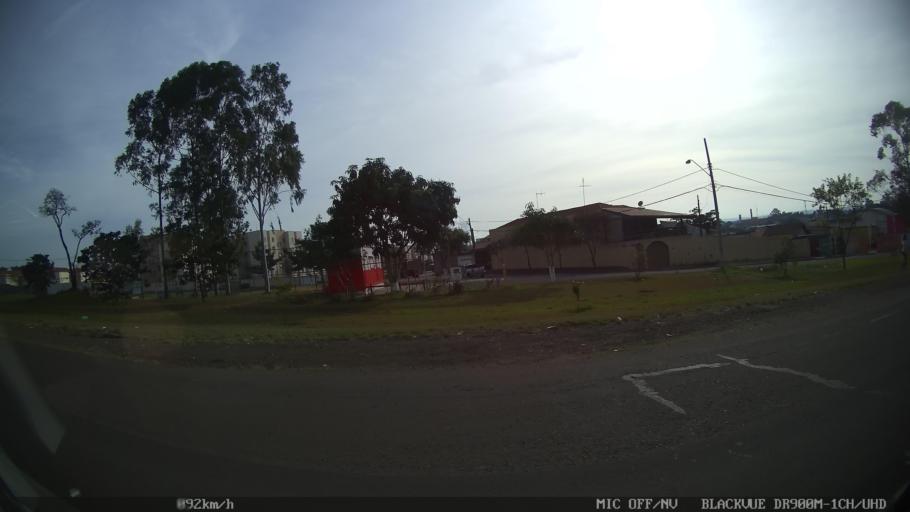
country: BR
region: Sao Paulo
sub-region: Piracicaba
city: Piracicaba
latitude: -22.6818
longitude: -47.6931
